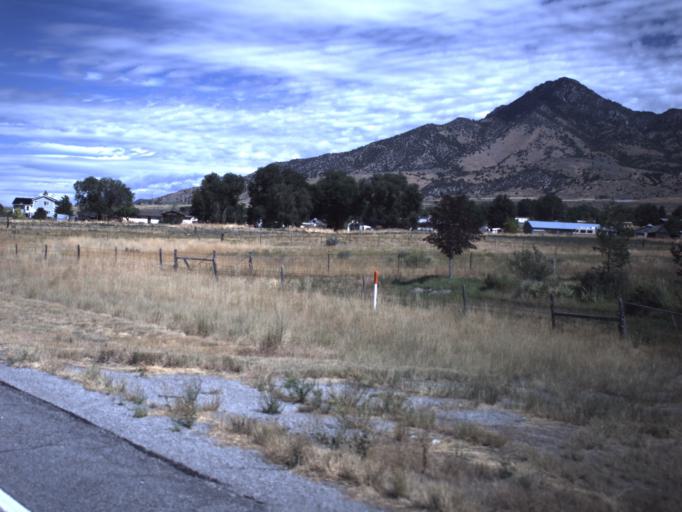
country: US
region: Utah
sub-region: Box Elder County
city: Garland
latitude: 41.8745
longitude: -112.1499
